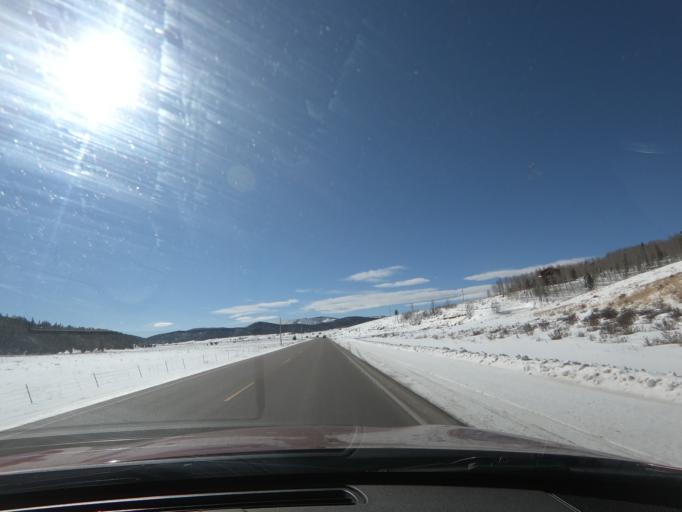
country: US
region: Colorado
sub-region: Teller County
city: Cripple Creek
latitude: 38.7946
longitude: -105.1238
